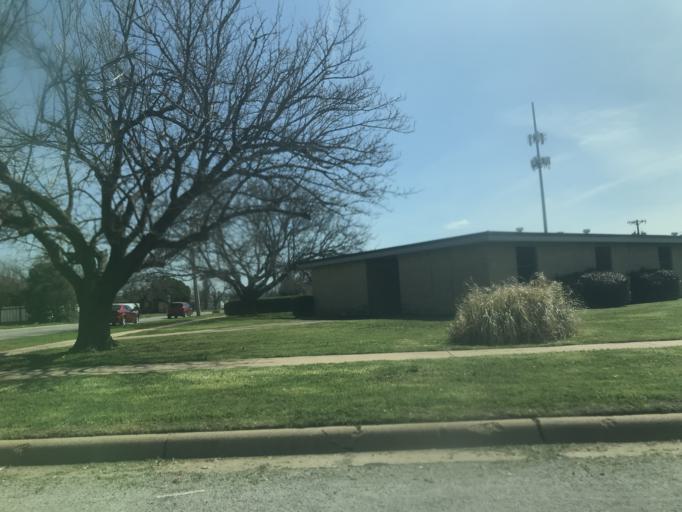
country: US
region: Texas
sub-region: Taylor County
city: Abilene
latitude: 32.4669
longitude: -99.7423
